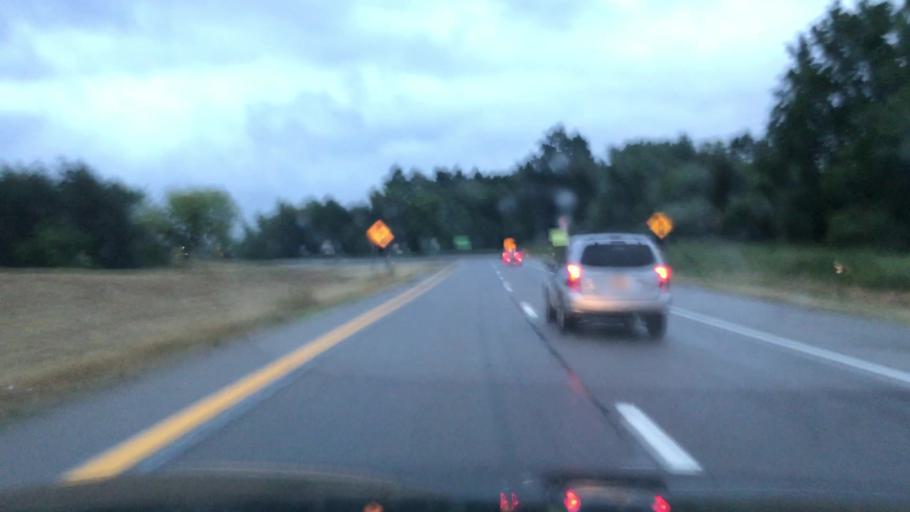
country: US
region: Michigan
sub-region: Kent County
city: East Grand Rapids
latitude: 42.9728
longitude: -85.5941
